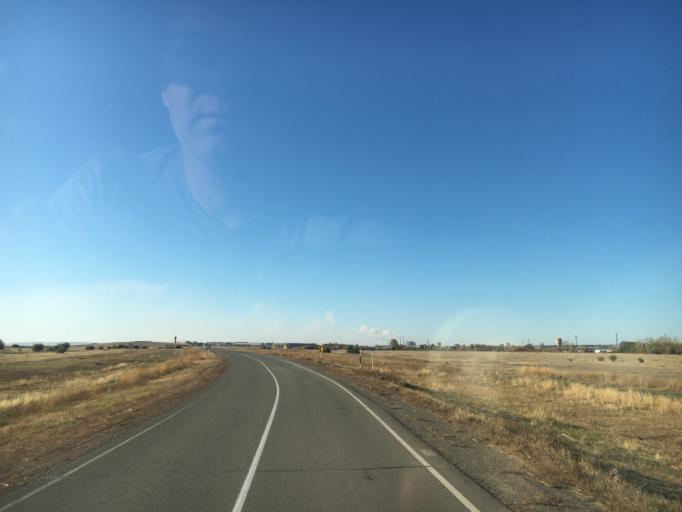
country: KZ
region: Qaraghandy
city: Aqtau
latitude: 50.1954
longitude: 73.0919
